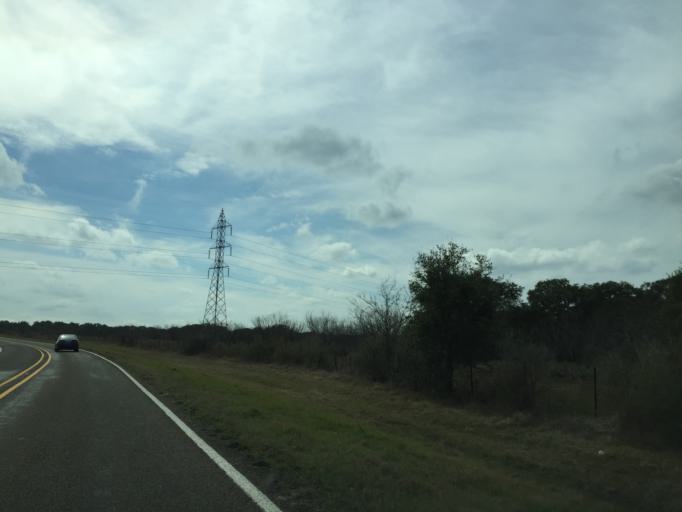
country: US
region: Texas
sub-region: Burnet County
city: Granite Shoals
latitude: 30.5253
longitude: -98.4474
